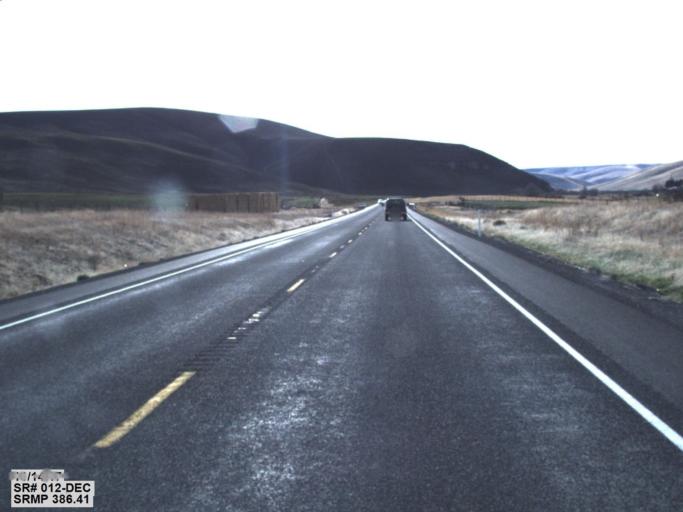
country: US
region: Washington
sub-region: Columbia County
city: Dayton
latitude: 46.5389
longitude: -117.9014
